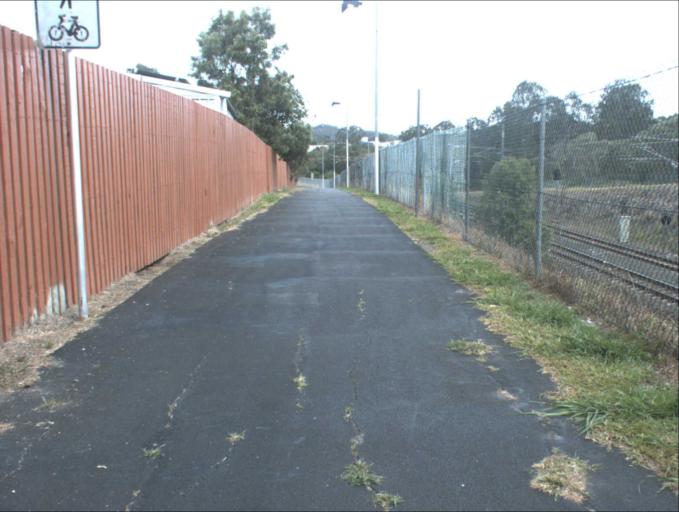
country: AU
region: Queensland
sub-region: Logan
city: Beenleigh
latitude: -27.7051
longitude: 153.1823
